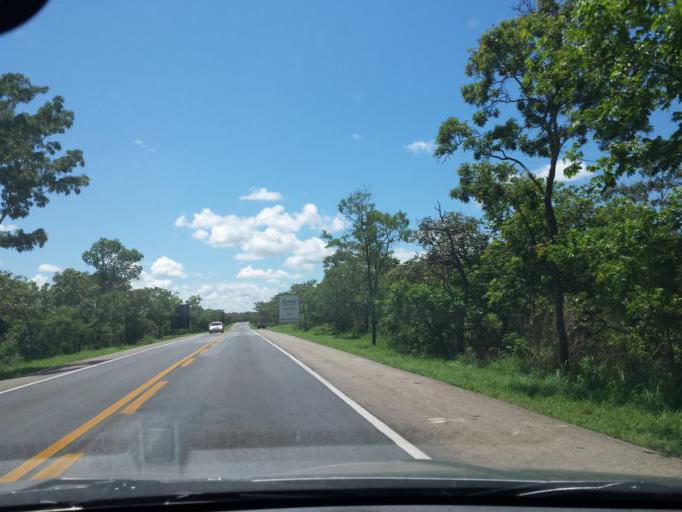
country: BR
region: Goias
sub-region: Luziania
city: Luziania
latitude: -16.4431
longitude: -47.8125
